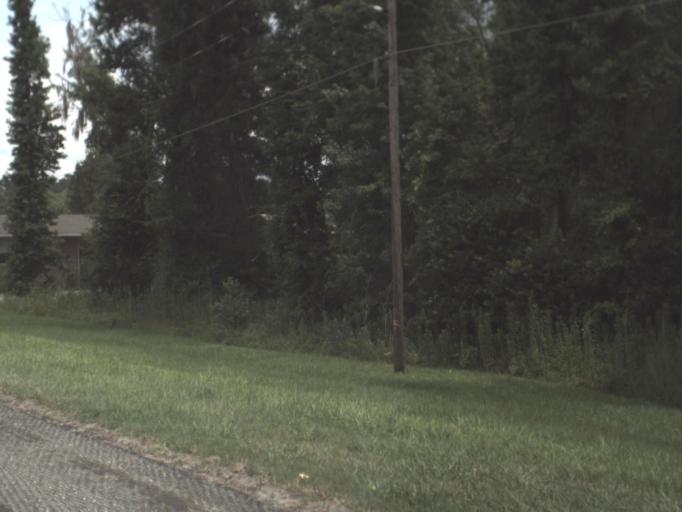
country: US
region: Florida
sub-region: Columbia County
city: Lake City
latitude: 30.1659
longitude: -82.6414
